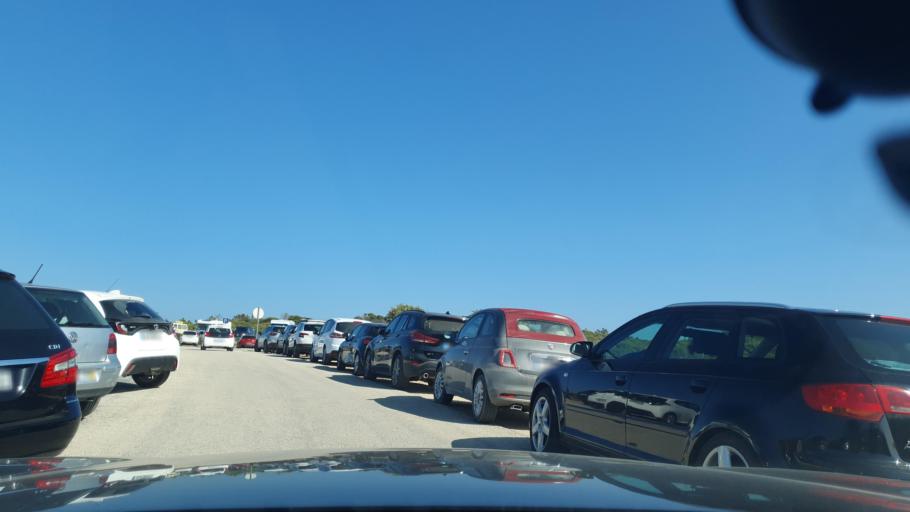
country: PT
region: Beja
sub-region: Odemira
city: Sao Teotonio
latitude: 37.4383
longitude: -8.7993
